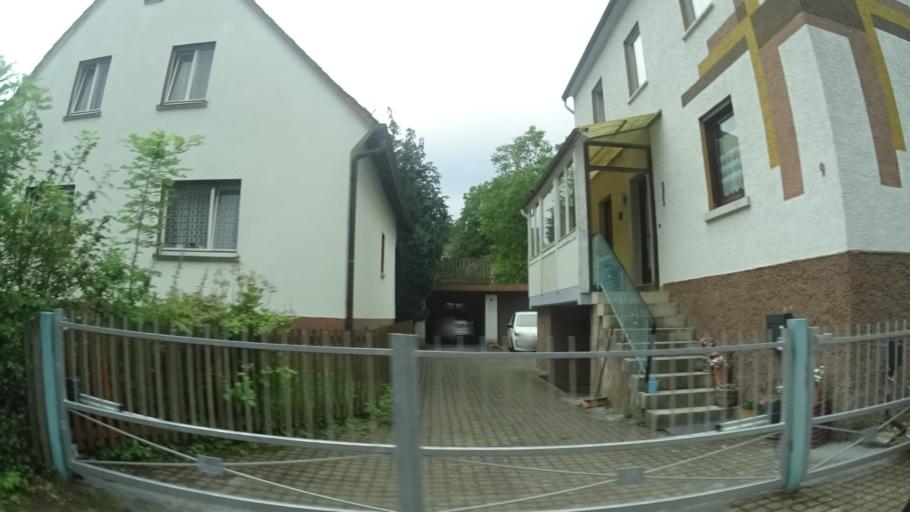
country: DE
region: Bavaria
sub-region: Regierungsbezirk Unterfranken
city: Johannesberg
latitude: 50.0601
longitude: 9.1285
